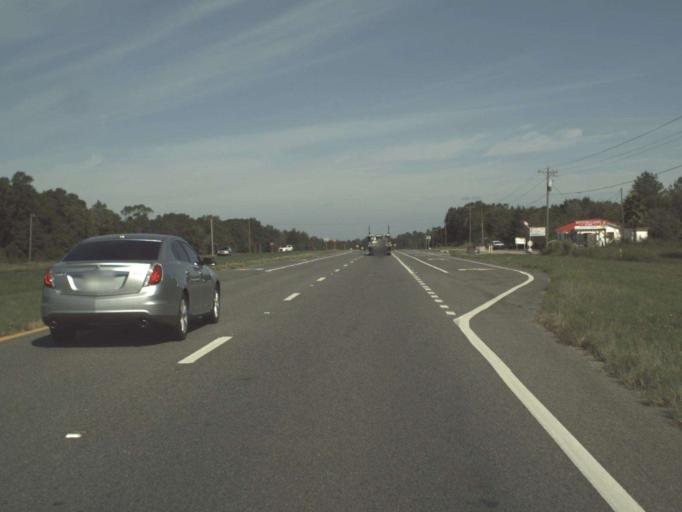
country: US
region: Florida
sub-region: Washington County
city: Chipley
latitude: 30.6368
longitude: -85.3992
